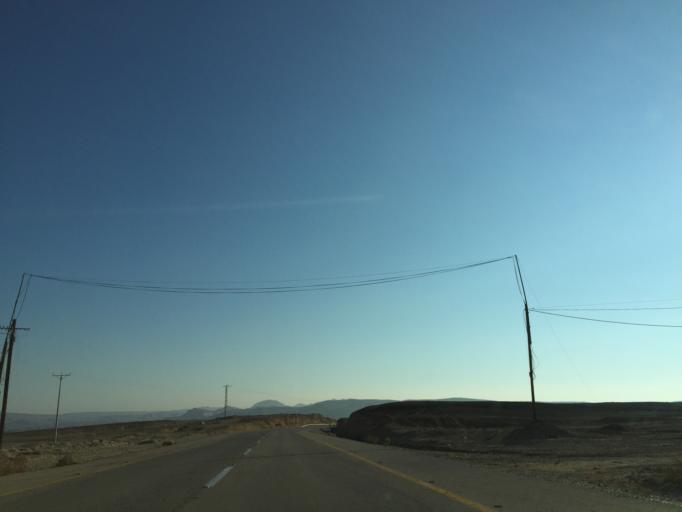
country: IL
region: Southern District
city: Mitzpe Ramon
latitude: 30.2892
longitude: 34.9918
